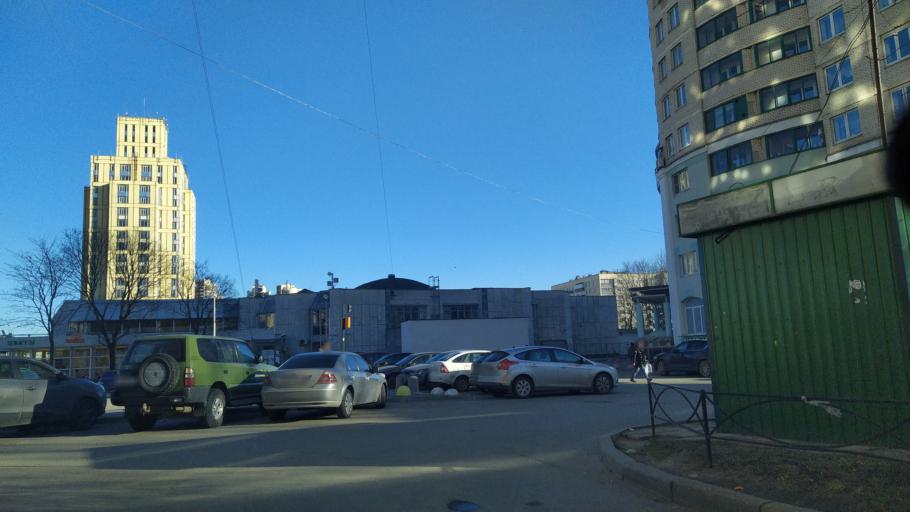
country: RU
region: St.-Petersburg
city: Grazhdanka
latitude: 60.0354
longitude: 30.4170
